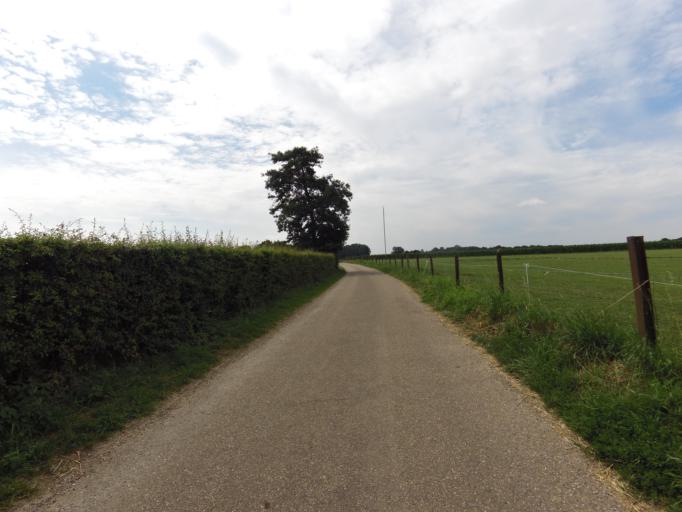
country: NL
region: Limburg
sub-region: Valkenburg aan de Geul
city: Schin op Geul
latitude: 50.8678
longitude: 5.8660
